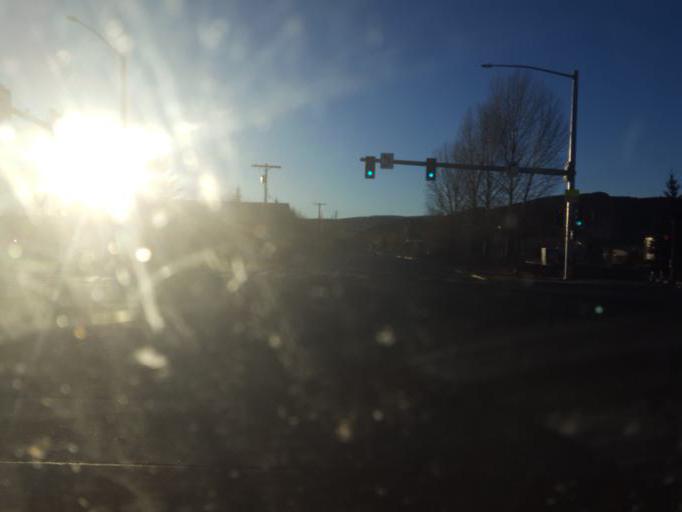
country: US
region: Colorado
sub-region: Gunnison County
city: Gunnison
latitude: 38.5552
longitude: -106.9266
